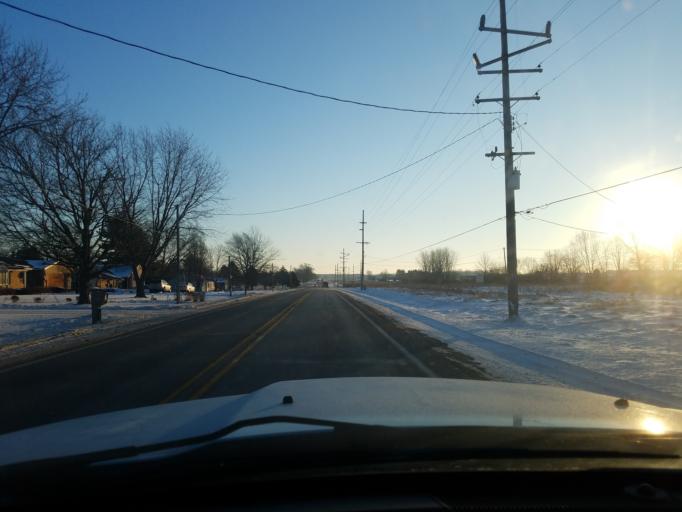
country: US
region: Indiana
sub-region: Marshall County
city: Bremen
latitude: 41.4538
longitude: -86.1240
